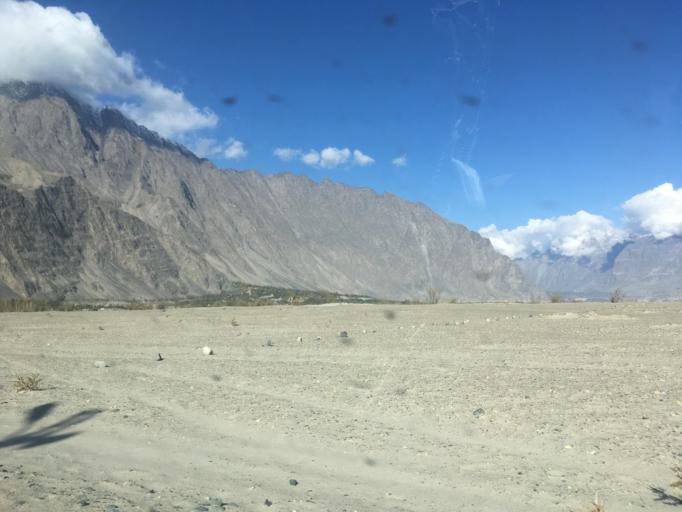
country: PK
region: Gilgit-Baltistan
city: Skardu
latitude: 35.3580
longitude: 75.5281
